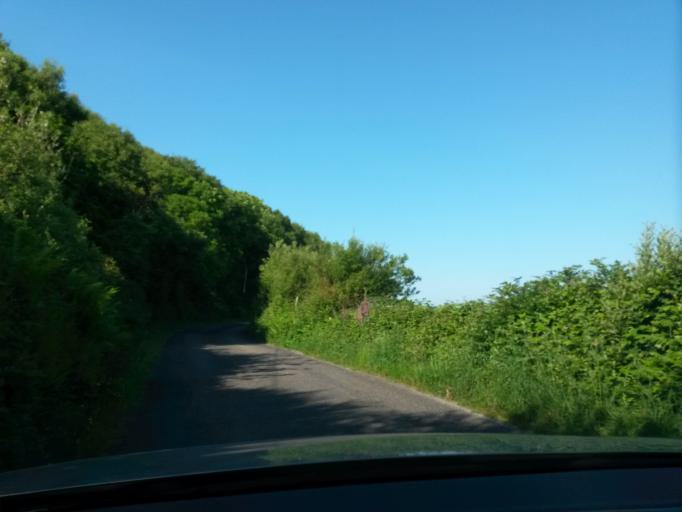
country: IE
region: Munster
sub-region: Ciarrai
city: Kenmare
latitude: 51.7939
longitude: -9.8005
